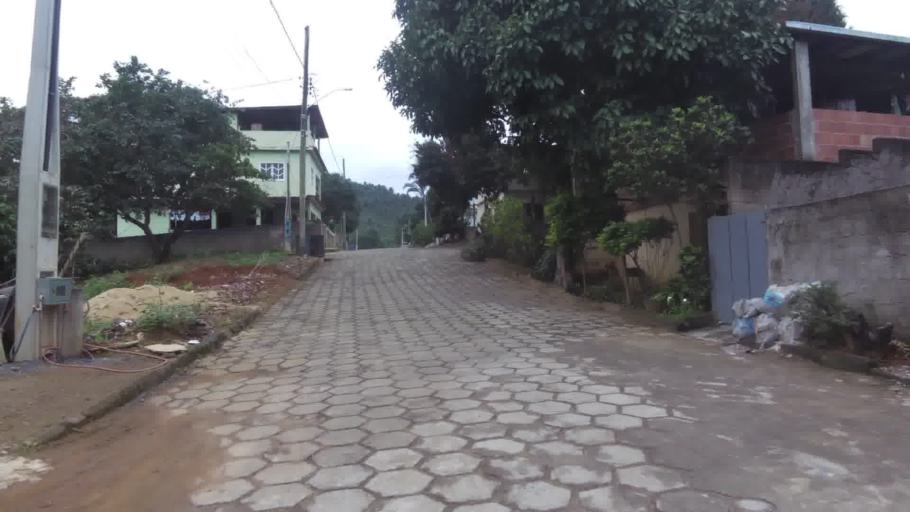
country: BR
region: Espirito Santo
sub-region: Iconha
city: Iconha
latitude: -20.7651
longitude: -40.8357
